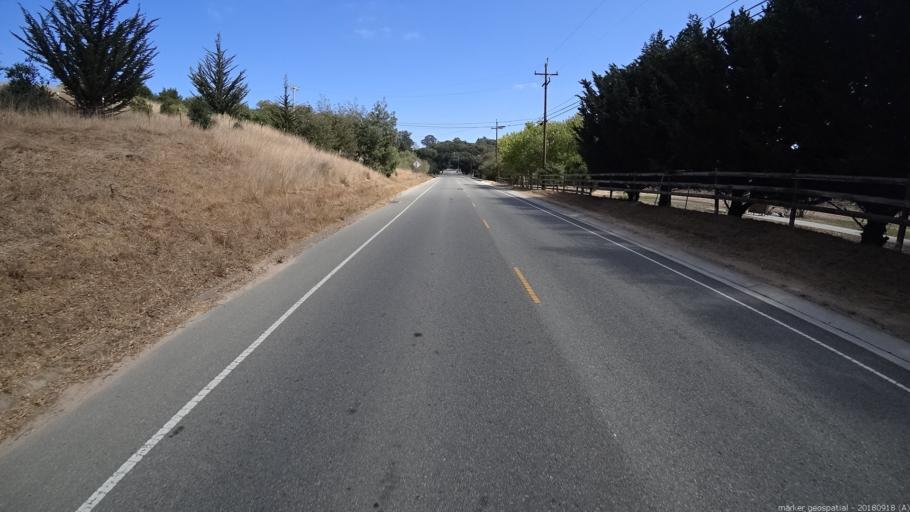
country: US
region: California
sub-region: Monterey County
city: Prunedale
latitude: 36.7726
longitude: -121.6641
